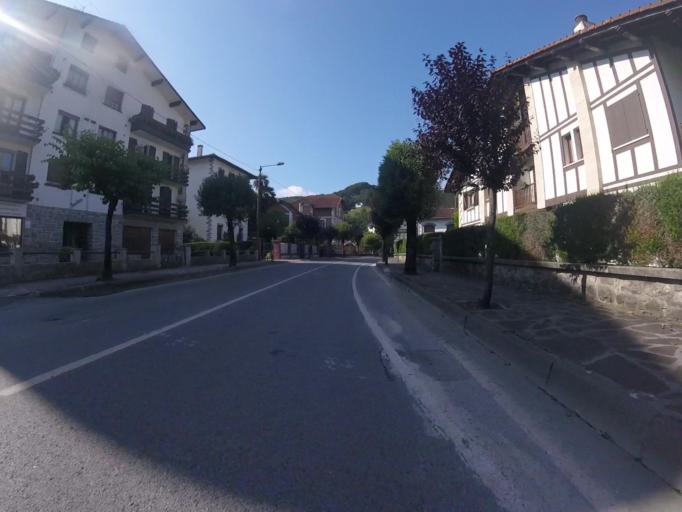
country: ES
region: Navarre
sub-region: Provincia de Navarra
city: Bera
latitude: 43.2785
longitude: -1.6887
